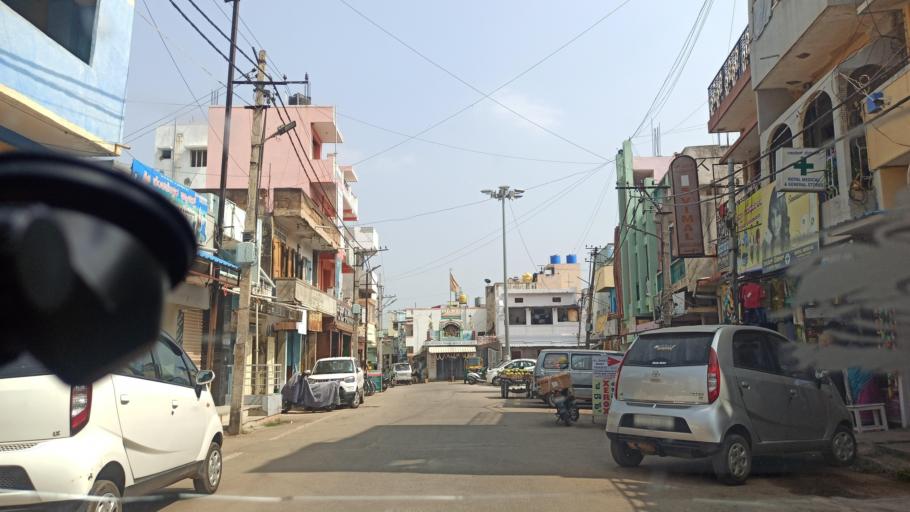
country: IN
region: Karnataka
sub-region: Bangalore Urban
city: Yelahanka
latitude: 13.1024
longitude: 77.5949
